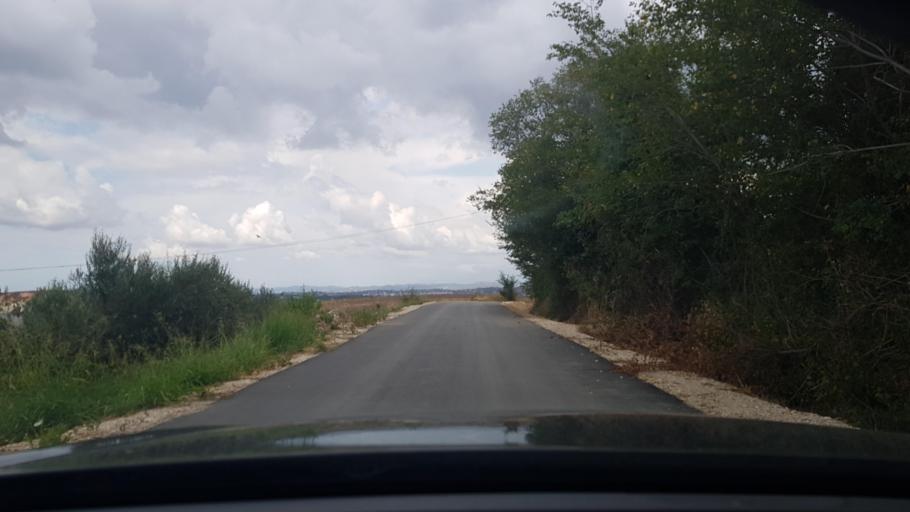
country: AL
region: Durres
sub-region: Rrethi i Durresit
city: Gjepalaj
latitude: 41.3045
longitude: 19.5539
